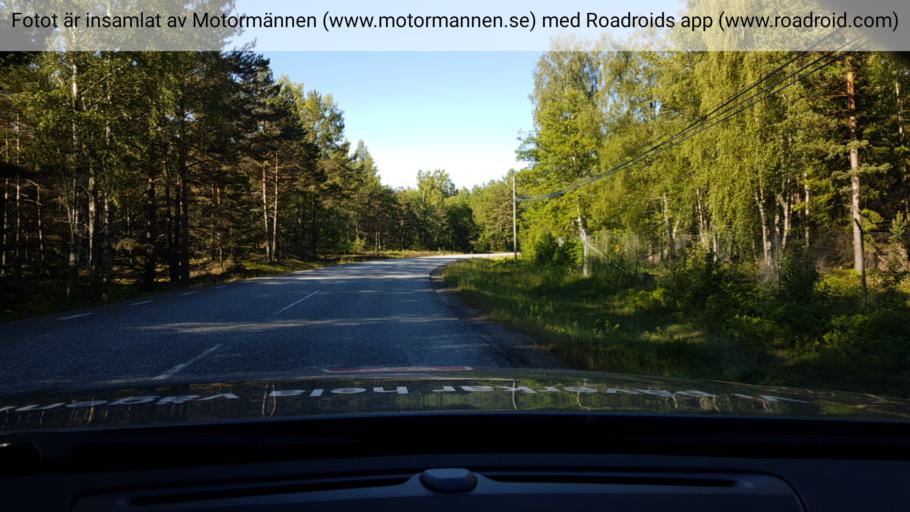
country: SE
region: Stockholm
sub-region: Nynashamns Kommun
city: Nynashamn
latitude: 58.9816
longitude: 18.0892
